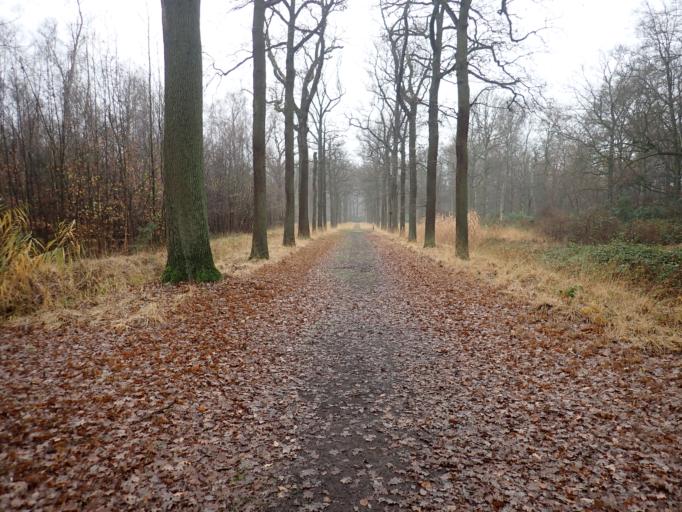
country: BE
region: Flanders
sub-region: Provincie Antwerpen
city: Schoten
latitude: 51.2657
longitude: 4.4907
